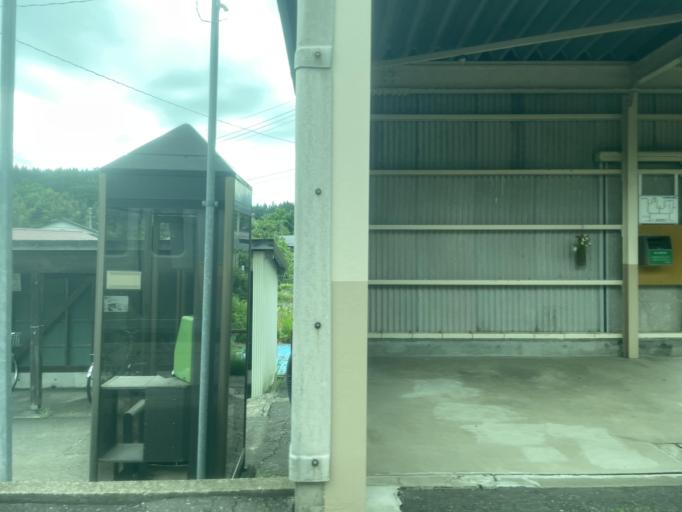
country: JP
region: Niigata
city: Nagaoka
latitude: 37.5156
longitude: 138.7041
